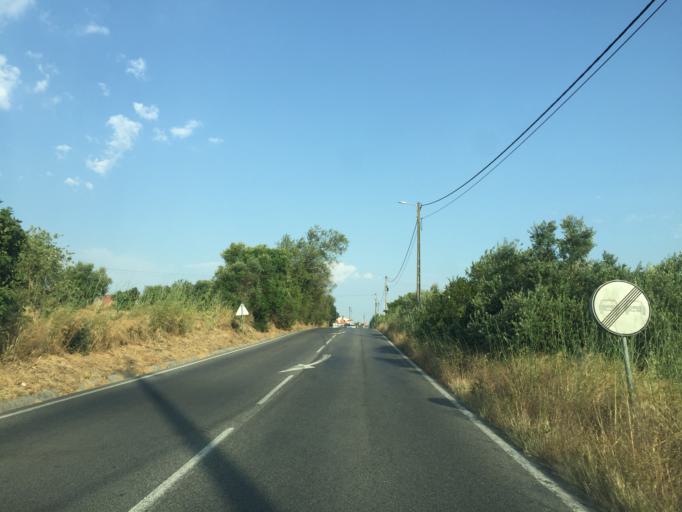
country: PT
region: Santarem
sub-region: Torres Novas
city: Torres Novas
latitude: 39.4796
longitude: -8.5720
